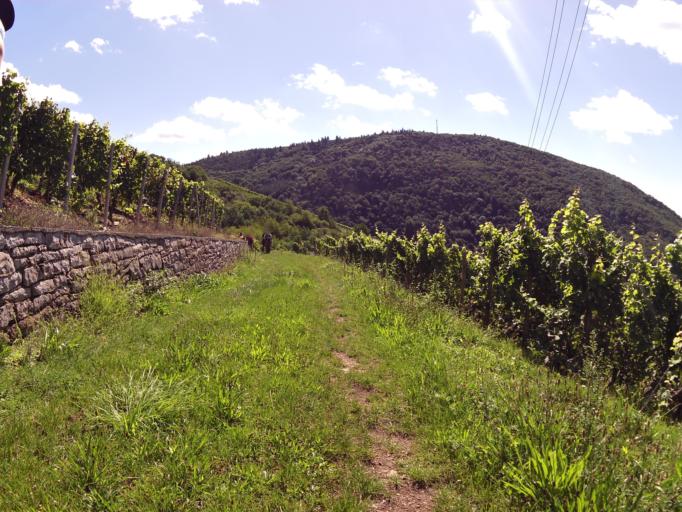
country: DE
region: Rheinland-Pfalz
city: Schlossbockelheim
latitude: 49.7948
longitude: 7.7631
